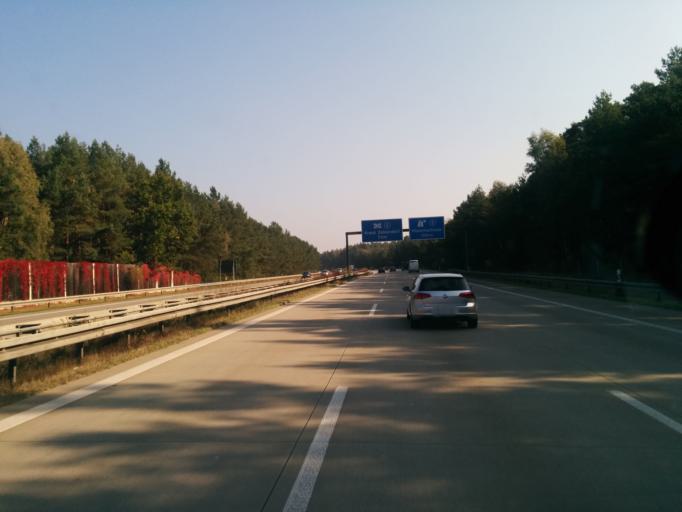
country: DE
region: Berlin
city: Wannsee
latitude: 52.3936
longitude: 13.1722
